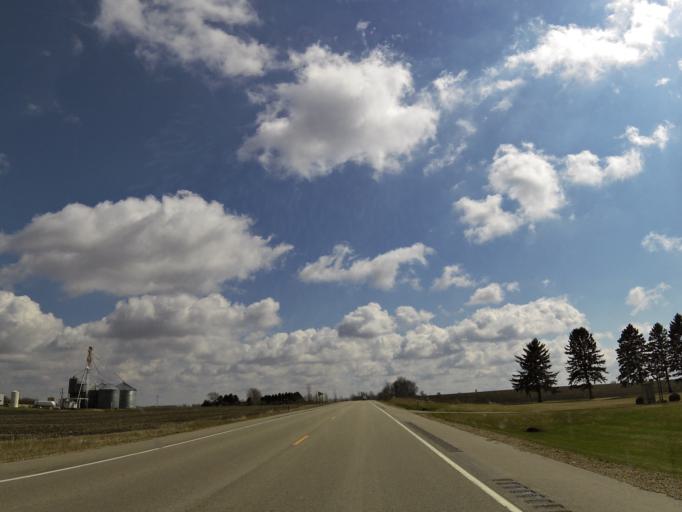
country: US
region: Minnesota
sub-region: Goodhue County
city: Kenyon
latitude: 44.1679
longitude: -92.9027
